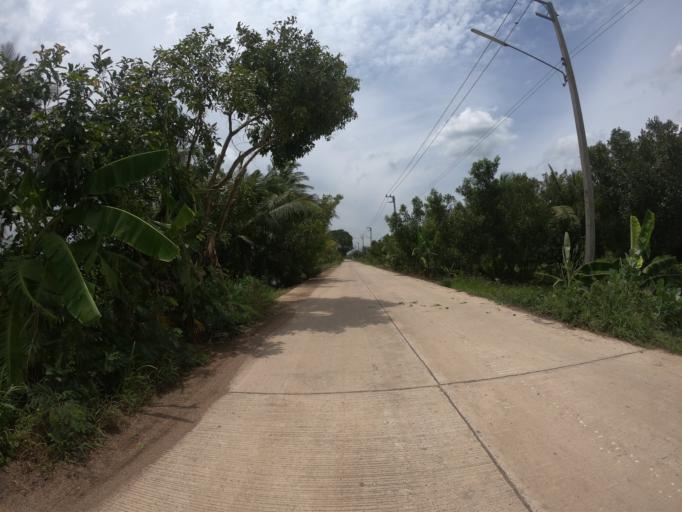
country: TH
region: Pathum Thani
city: Ban Lam Luk Ka
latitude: 14.0238
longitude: 100.8656
